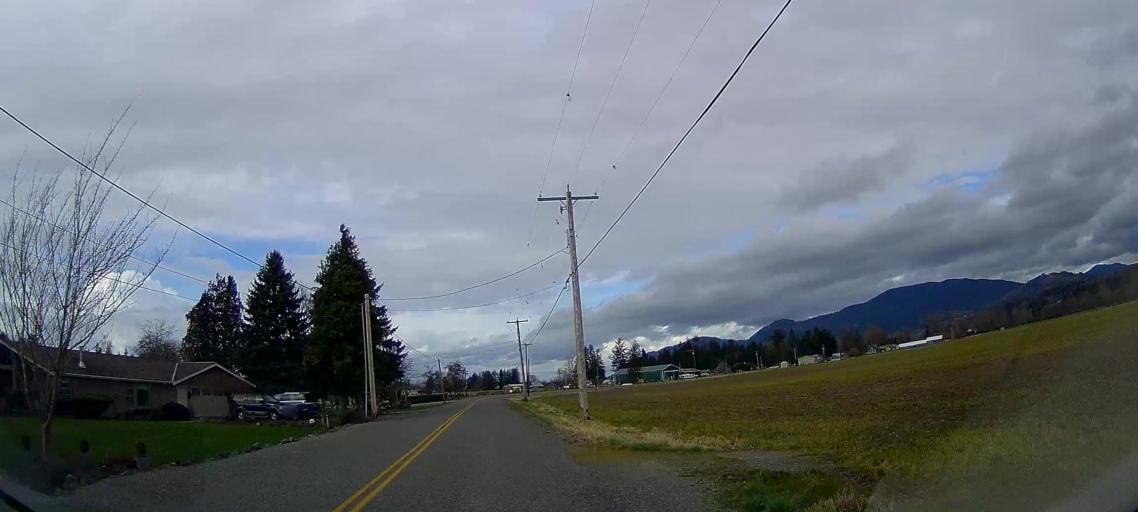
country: US
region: Washington
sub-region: Skagit County
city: Burlington
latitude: 48.5507
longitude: -122.3990
